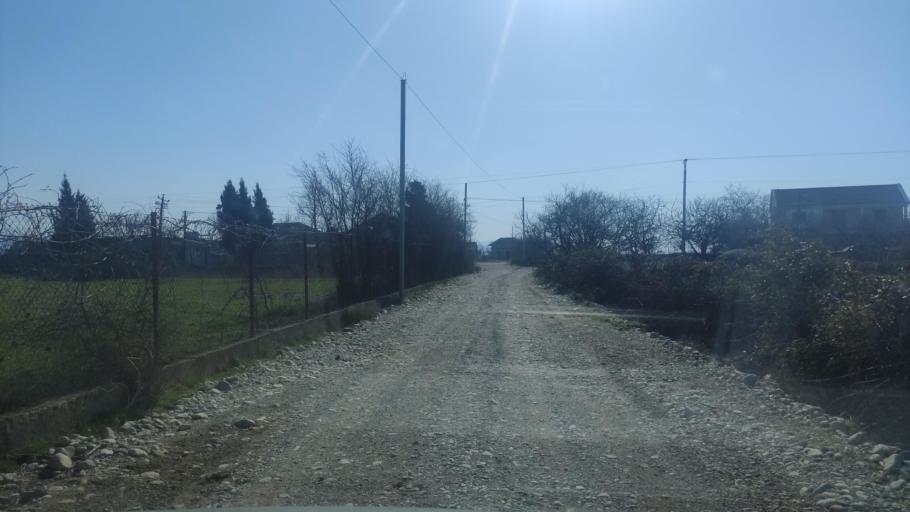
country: AL
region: Shkoder
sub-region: Rrethi i Malesia e Madhe
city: Grude-Fushe
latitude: 42.1620
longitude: 19.4574
